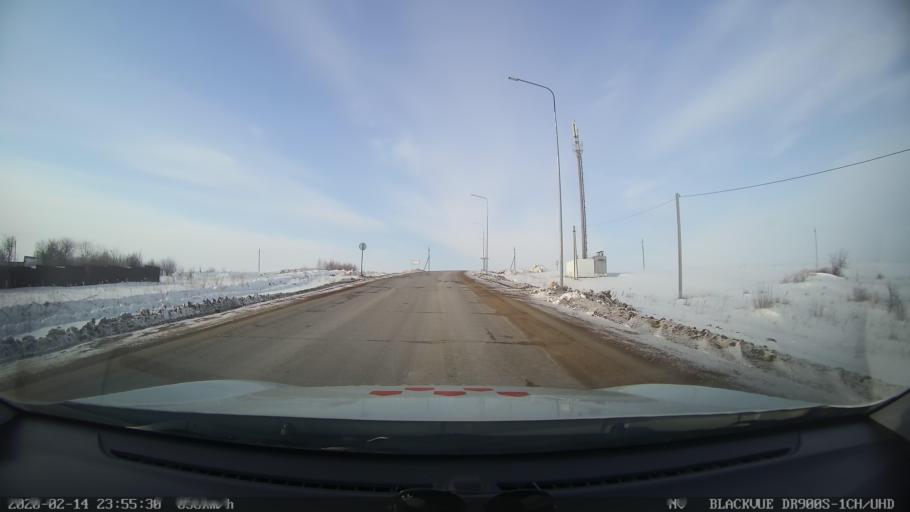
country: RU
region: Tatarstan
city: Kuybyshevskiy Zaton
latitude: 55.3170
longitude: 49.1425
